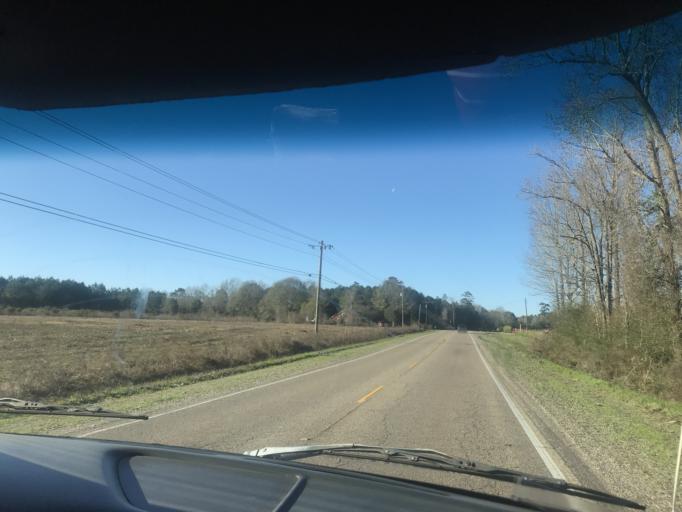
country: US
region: Louisiana
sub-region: Saint Tammany Parish
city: Covington
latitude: 30.5966
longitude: -90.1771
